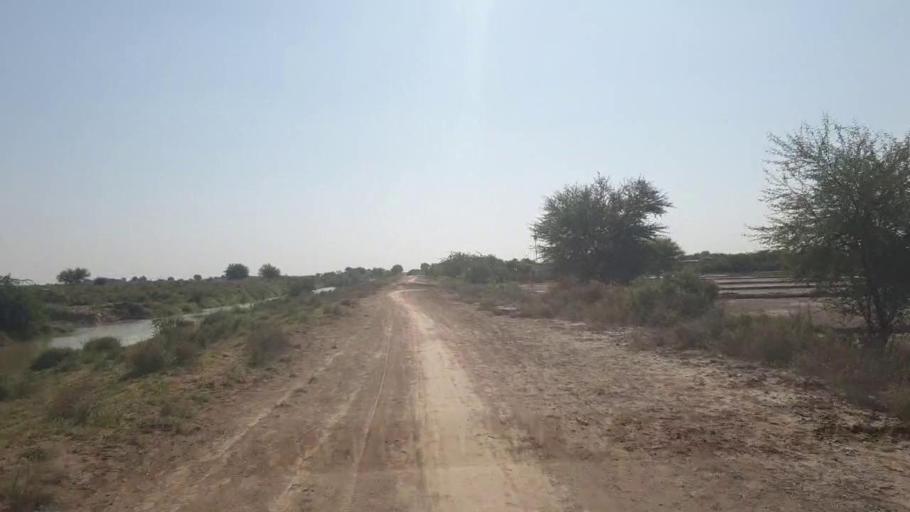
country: PK
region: Sindh
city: Tando Bago
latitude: 24.8918
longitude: 69.1645
